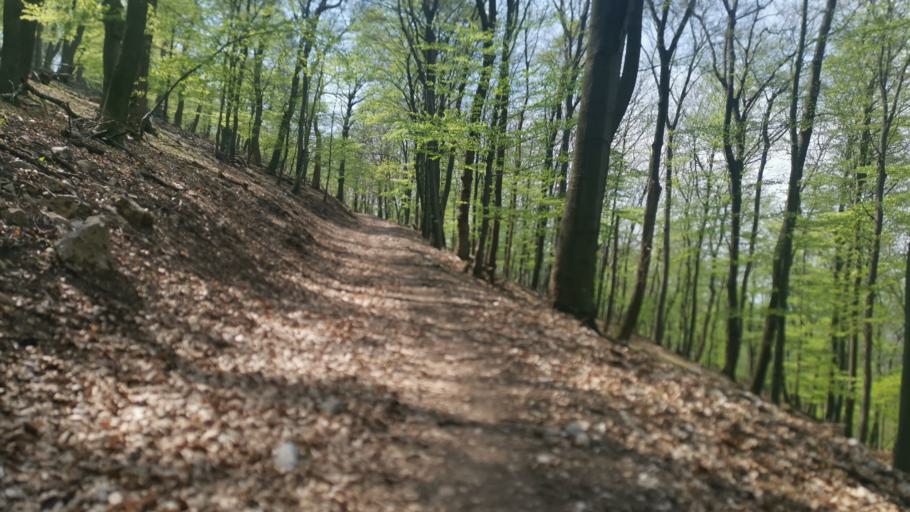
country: SK
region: Trnavsky
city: Smolenice
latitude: 48.5298
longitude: 17.4130
